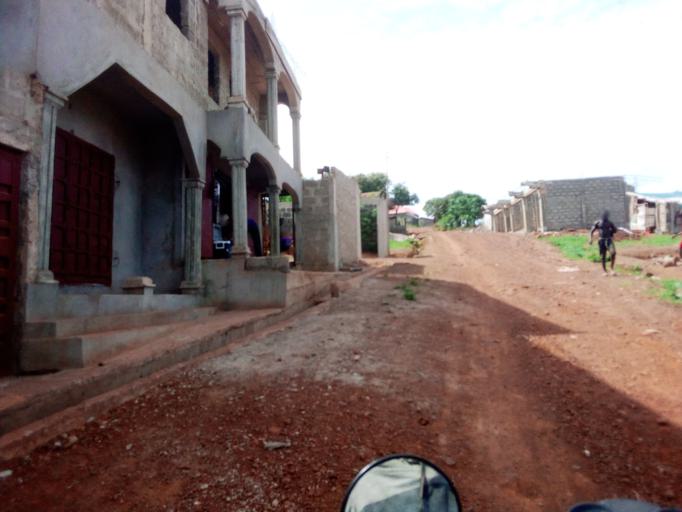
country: SL
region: Western Area
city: Waterloo
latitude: 8.3406
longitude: -13.0815
